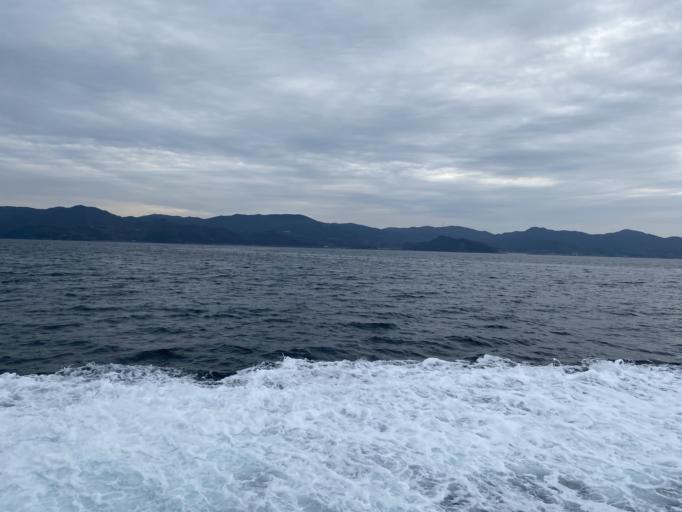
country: JP
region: Nagasaki
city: Nagasaki-shi
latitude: 32.6390
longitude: 129.7610
